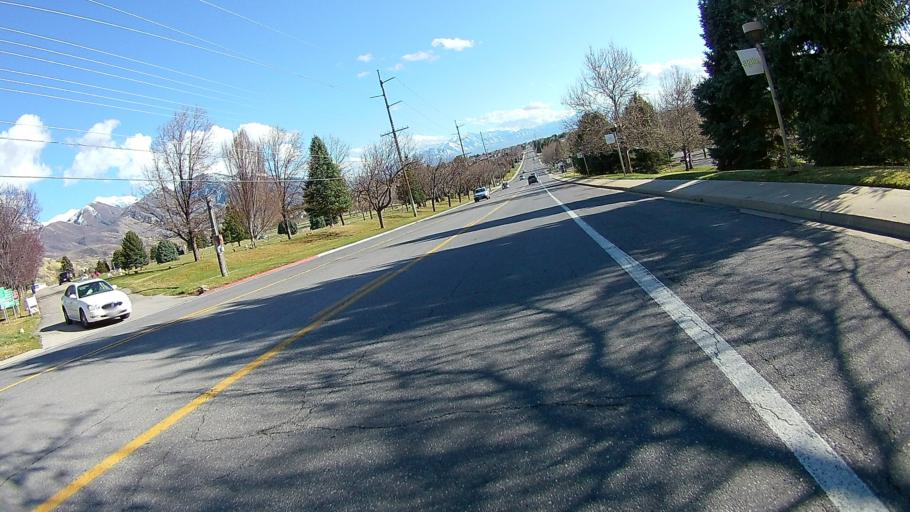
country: US
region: Utah
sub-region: Utah County
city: Orem
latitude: 40.3248
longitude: -111.6769
